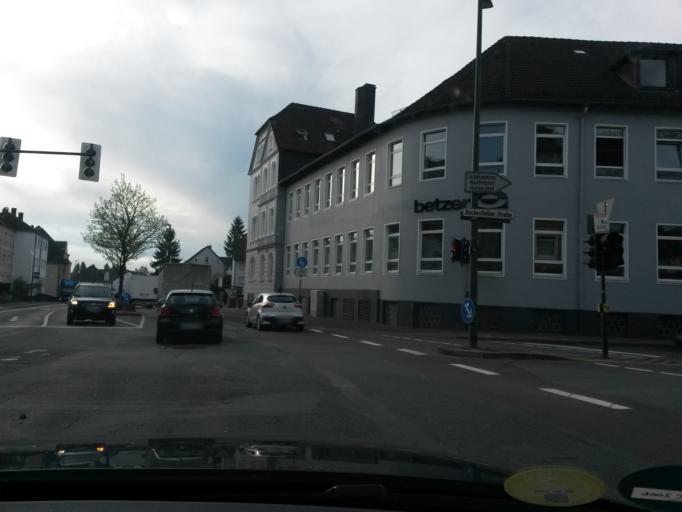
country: DE
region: North Rhine-Westphalia
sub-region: Regierungsbezirk Arnsberg
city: Luedenscheid
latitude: 51.2269
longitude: 7.6133
